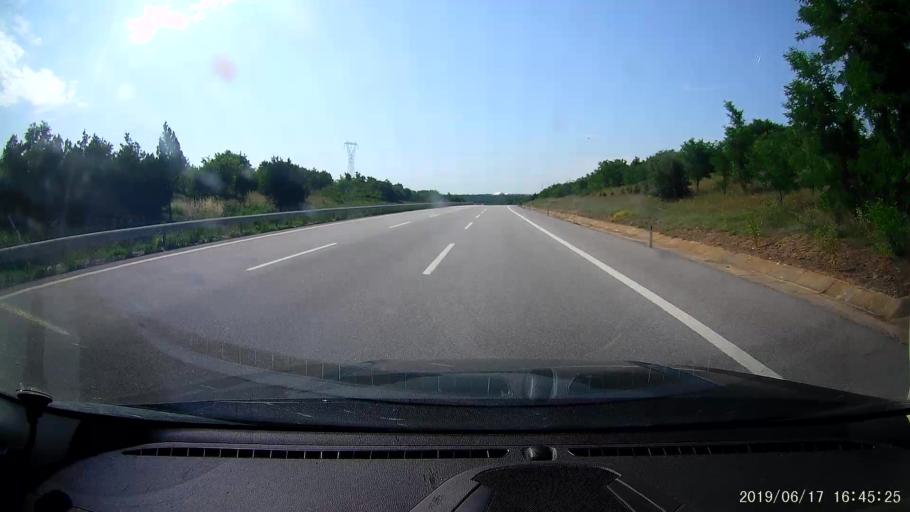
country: TR
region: Kirklareli
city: Babaeski
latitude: 41.4882
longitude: 27.2330
